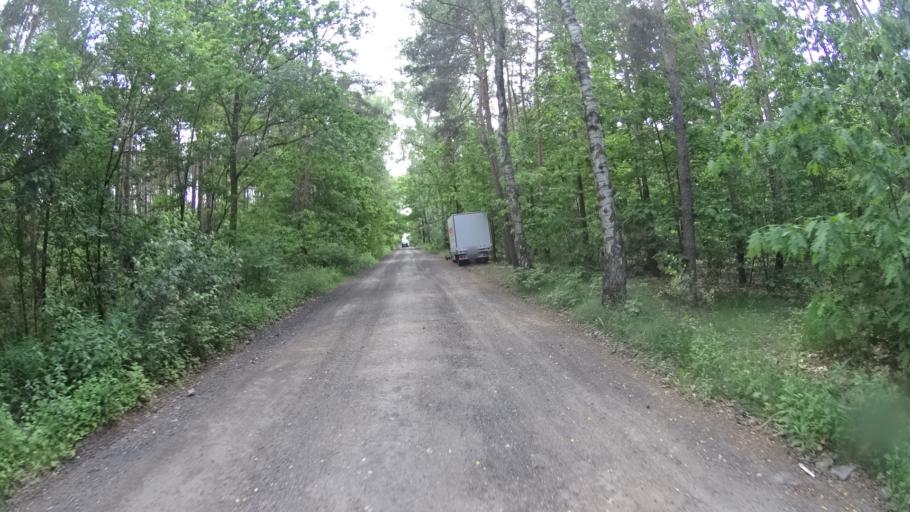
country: PL
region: Masovian Voivodeship
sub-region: Powiat pruszkowski
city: Nadarzyn
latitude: 52.0656
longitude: 20.8204
